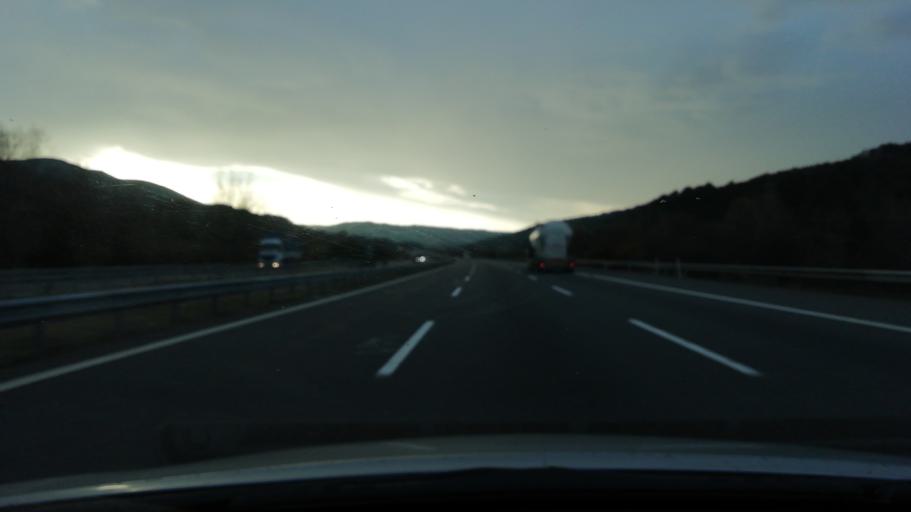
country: TR
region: Bolu
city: Yenicaga
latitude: 40.7435
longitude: 31.8623
